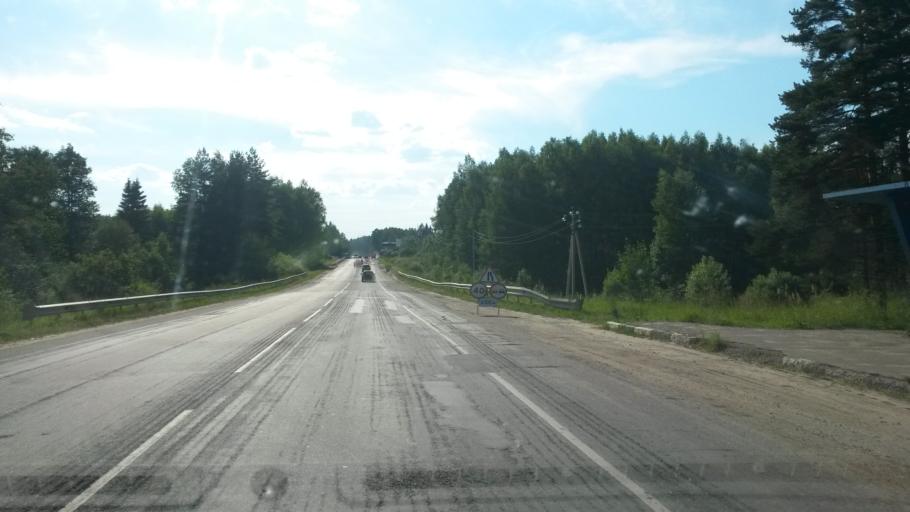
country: RU
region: Ivanovo
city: Kokhma
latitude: 56.9978
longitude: 41.1549
